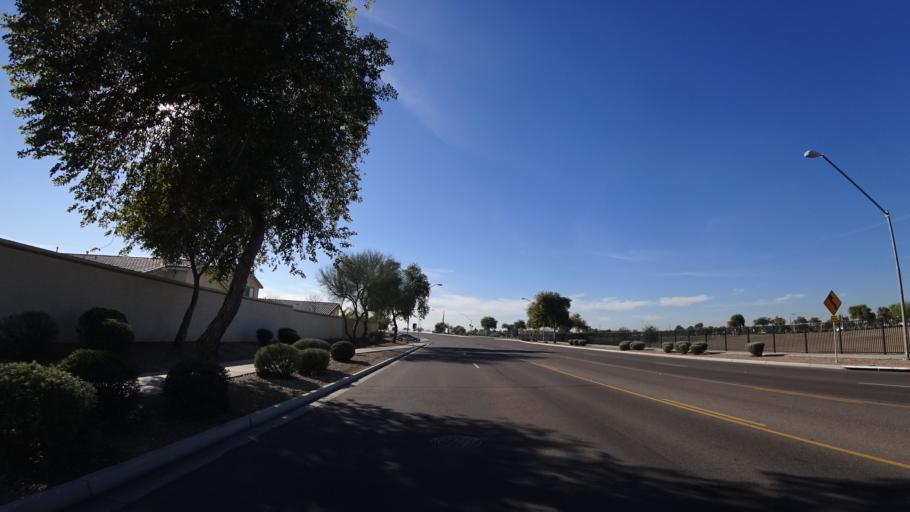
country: US
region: Arizona
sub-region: Maricopa County
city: Glendale
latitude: 33.5233
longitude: -112.2324
